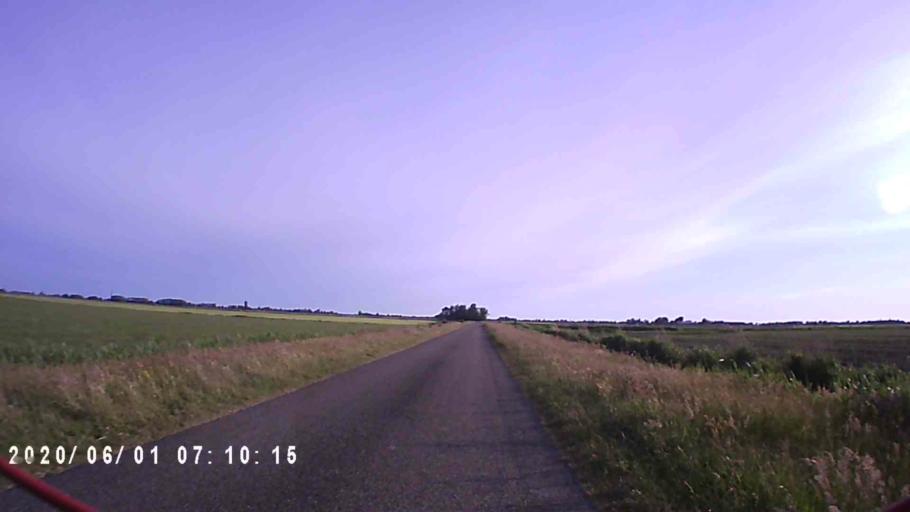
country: NL
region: Friesland
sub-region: Gemeente Dantumadiel
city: Walterswald
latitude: 53.3132
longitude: 6.0685
